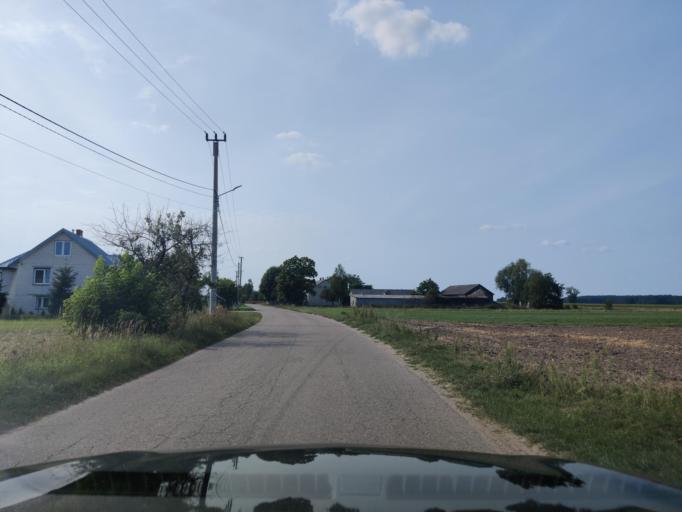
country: PL
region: Masovian Voivodeship
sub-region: Powiat wyszkowski
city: Rzasnik
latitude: 52.7390
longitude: 21.3404
